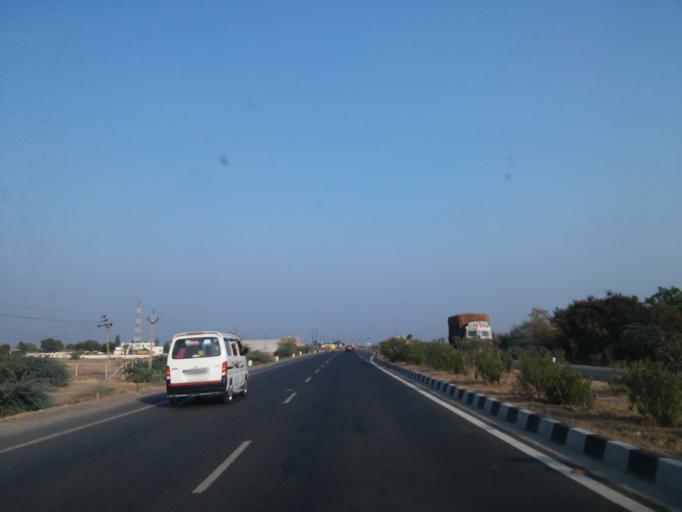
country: IN
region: Gujarat
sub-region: Ahmadabad
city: Mandal
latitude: 23.0980
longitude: 72.0654
